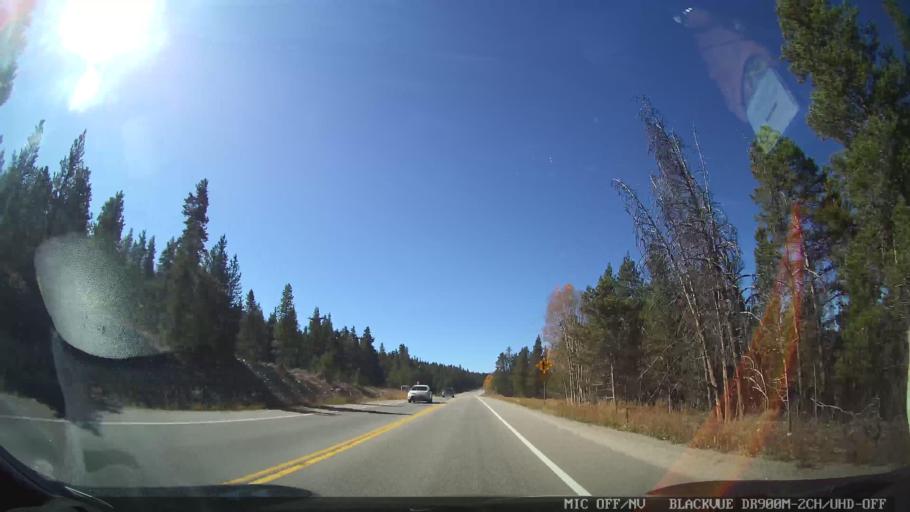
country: US
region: Colorado
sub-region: Lake County
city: Leadville North
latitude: 39.2780
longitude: -106.2823
